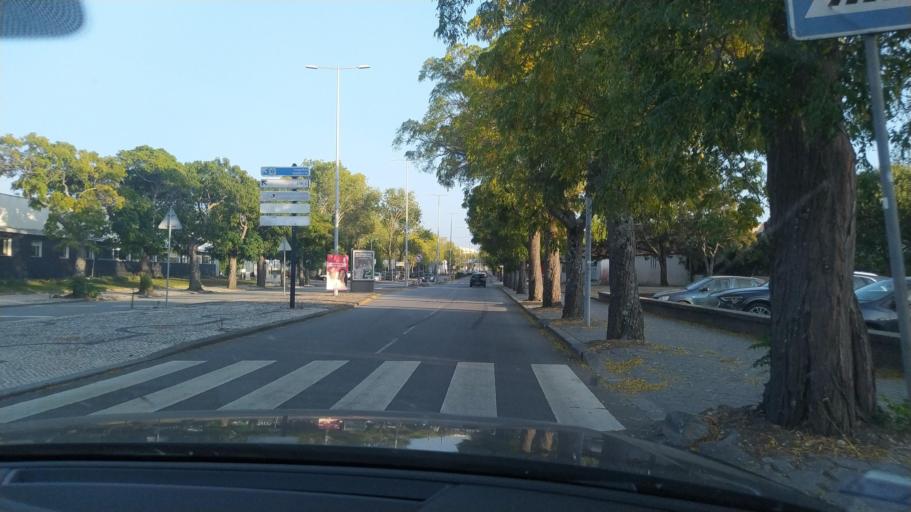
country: PT
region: Aveiro
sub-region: Aveiro
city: Aveiro
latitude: 40.6339
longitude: -8.6563
